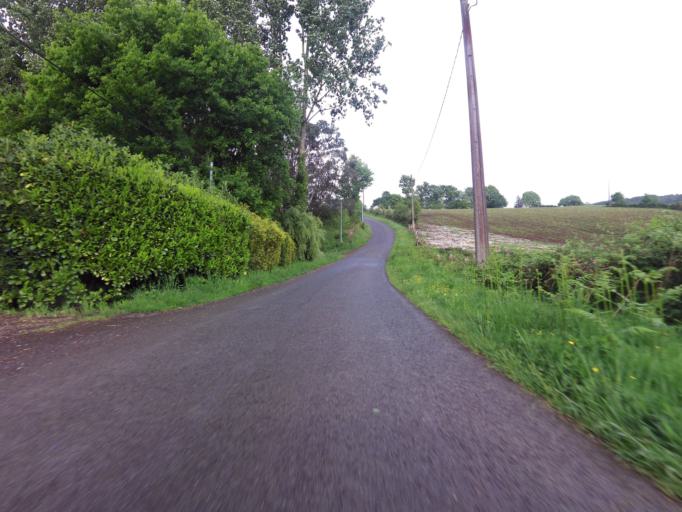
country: FR
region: Brittany
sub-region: Departement du Morbihan
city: Pluherlin
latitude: 47.7131
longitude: -2.3606
